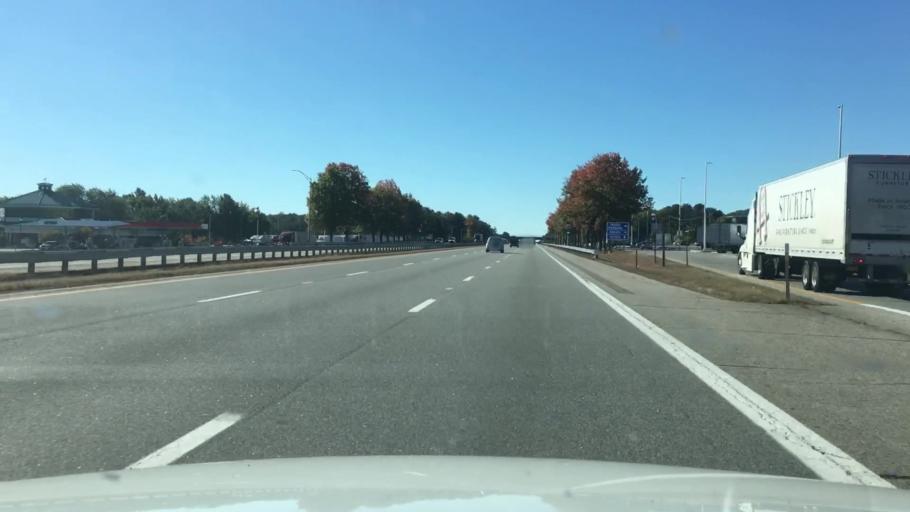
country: US
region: Maine
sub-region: York County
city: West Kennebunk
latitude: 43.4124
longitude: -70.5587
